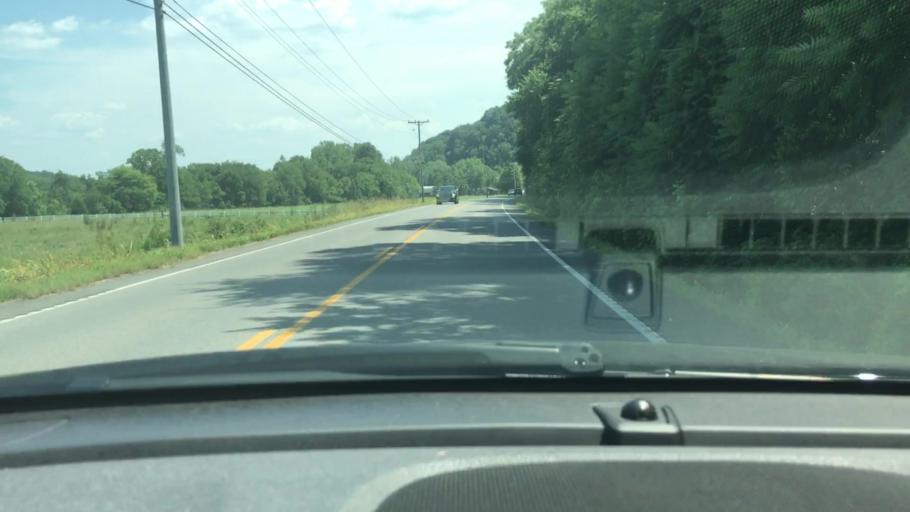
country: US
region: Tennessee
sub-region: Sumner County
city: Shackle Island
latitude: 36.3994
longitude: -86.6299
